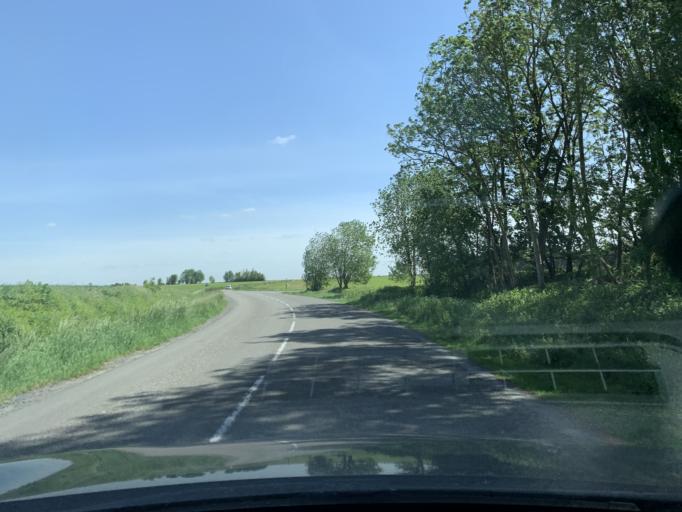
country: FR
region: Nord-Pas-de-Calais
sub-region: Departement du Nord
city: Marcoing
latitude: 50.1375
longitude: 3.1934
